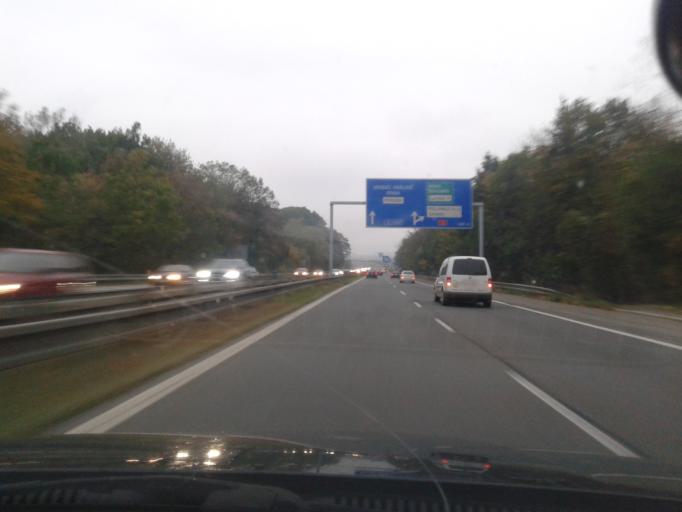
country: CZ
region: Moravskoslezsky
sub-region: Okres Ostrava-Mesto
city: Ostrava
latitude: 49.8021
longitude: 18.2179
